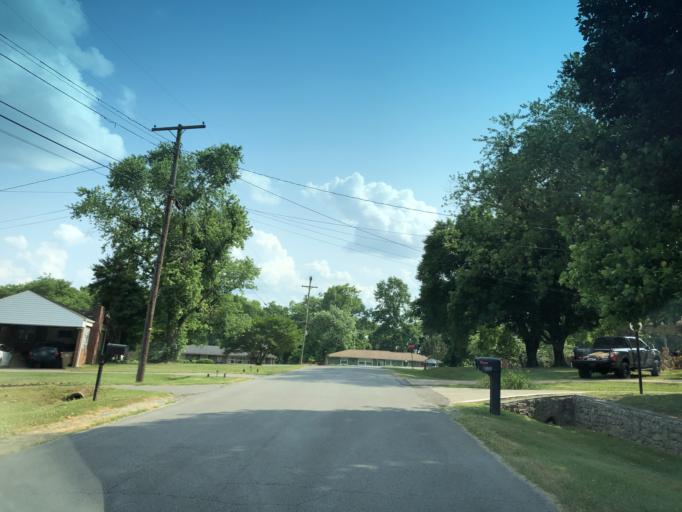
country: US
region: Tennessee
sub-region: Davidson County
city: Goodlettsville
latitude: 36.2538
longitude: -86.7258
